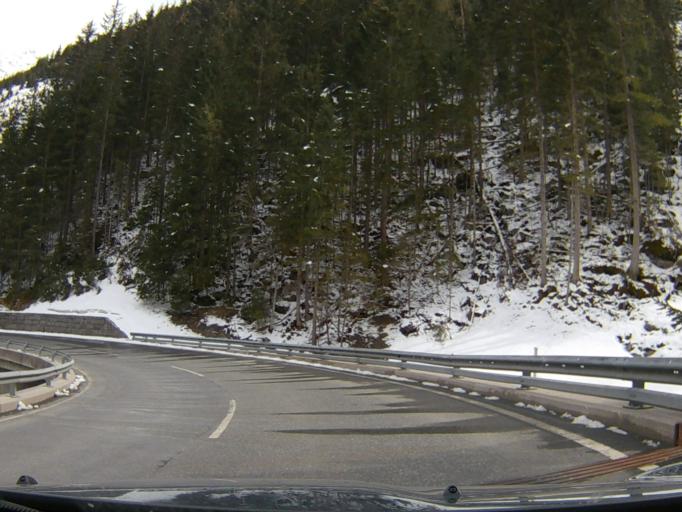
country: AT
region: Salzburg
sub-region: Politischer Bezirk Zell am See
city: Krimml
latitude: 47.2189
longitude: 12.1574
